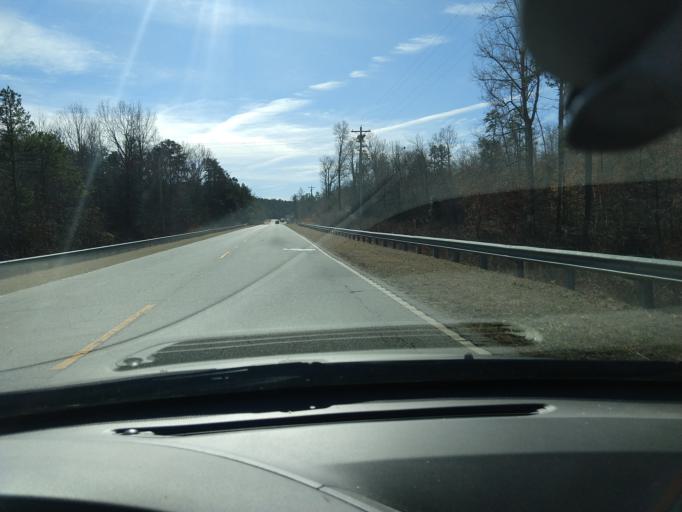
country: US
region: South Carolina
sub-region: Oconee County
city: Westminster
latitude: 34.6281
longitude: -83.1362
